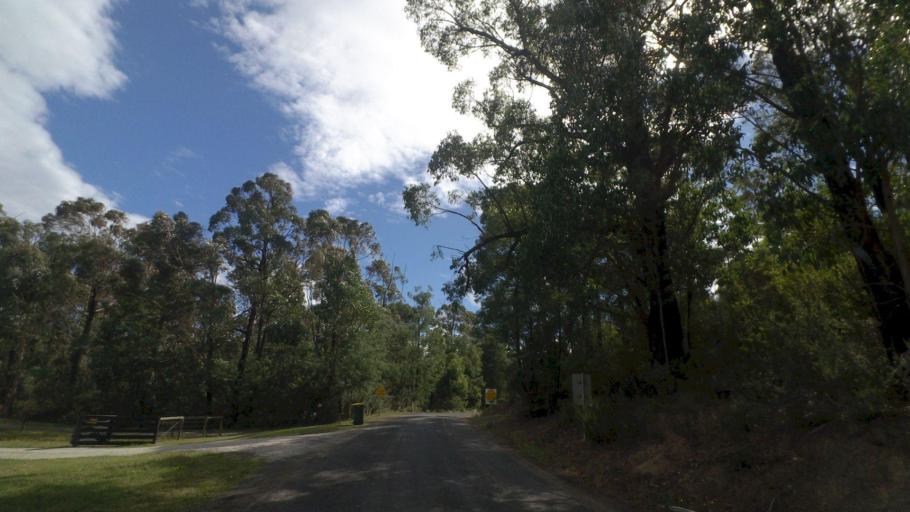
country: AU
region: Victoria
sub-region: Cardinia
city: Bunyip
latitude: -38.0196
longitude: 145.8096
